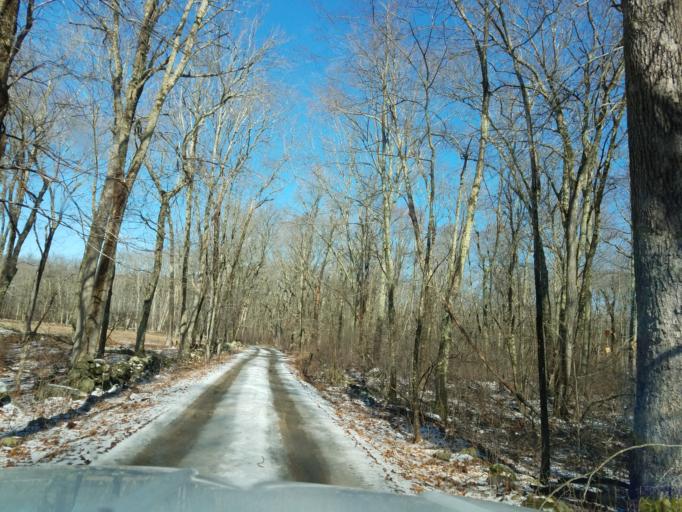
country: US
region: Connecticut
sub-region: New London County
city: Preston City
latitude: 41.4968
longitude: -71.9227
